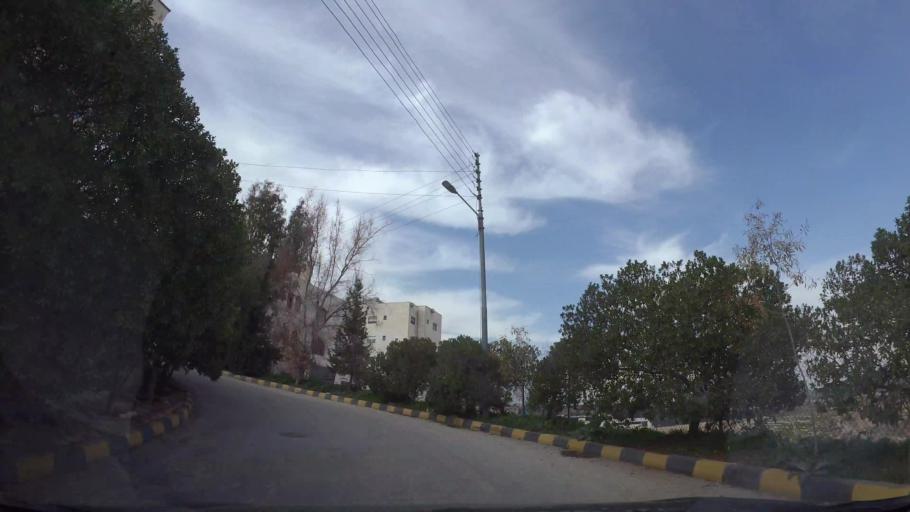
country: JO
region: Amman
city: Amman
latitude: 32.0129
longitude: 35.9450
